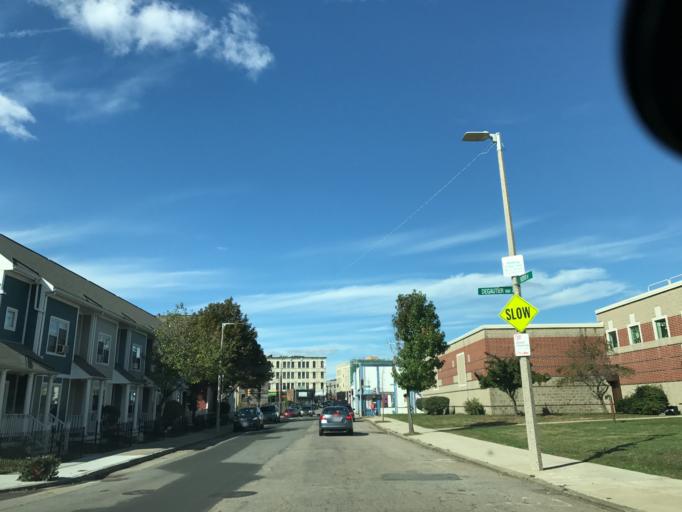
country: US
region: Massachusetts
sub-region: Suffolk County
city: South Boston
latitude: 42.3304
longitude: -71.0802
